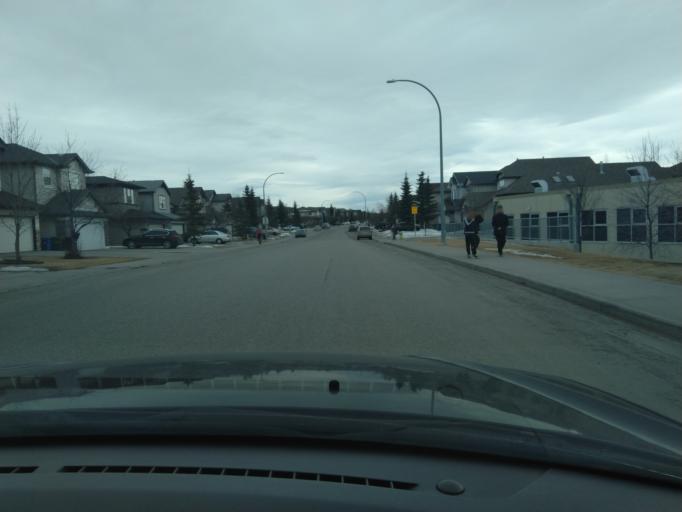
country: CA
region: Alberta
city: Calgary
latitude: 51.1624
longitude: -114.0877
